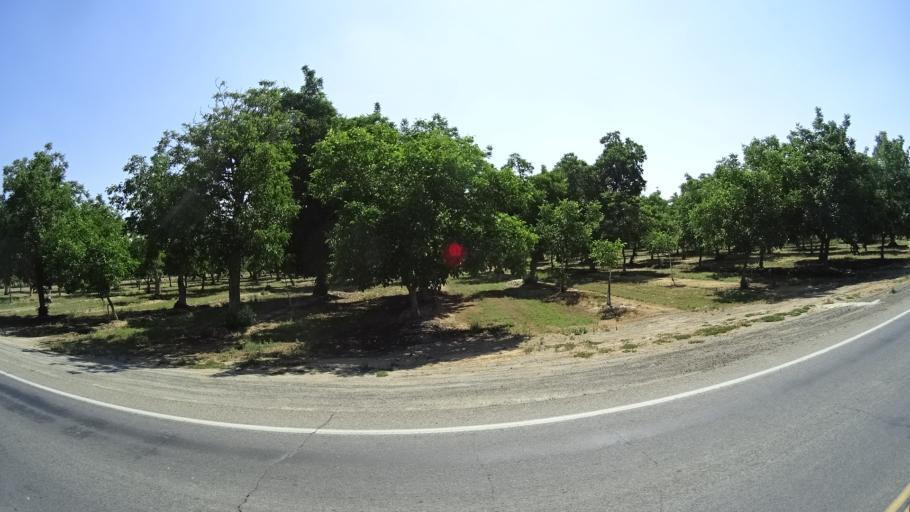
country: US
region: California
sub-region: Fresno County
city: Kingsburg
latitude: 36.4824
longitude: -119.5573
